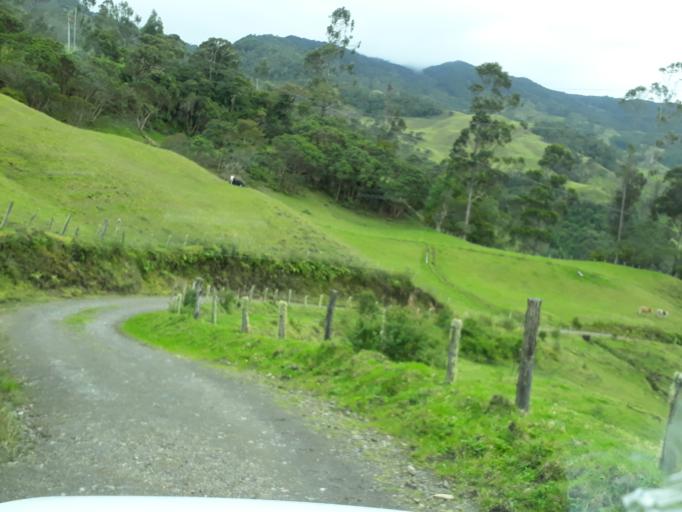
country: CO
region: Cundinamarca
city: Junin
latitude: 4.7426
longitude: -73.6263
